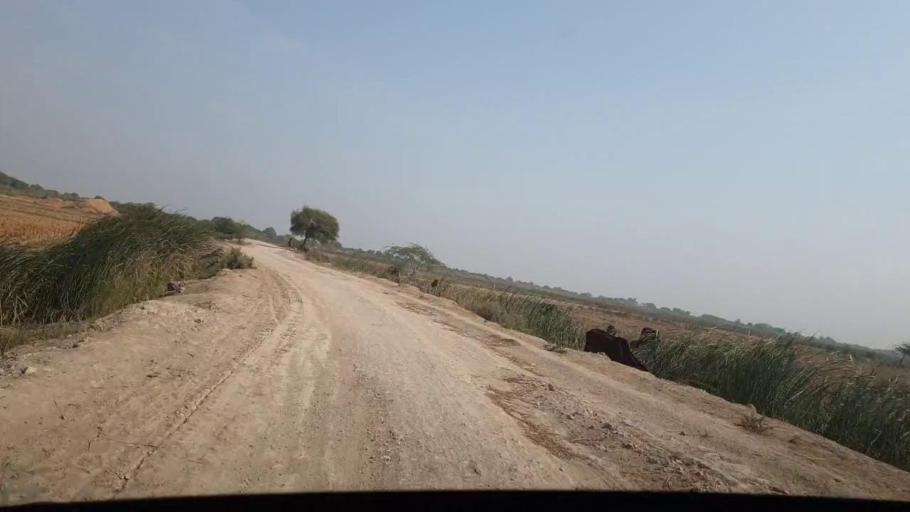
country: PK
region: Sindh
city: Chuhar Jamali
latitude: 24.2671
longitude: 67.9522
